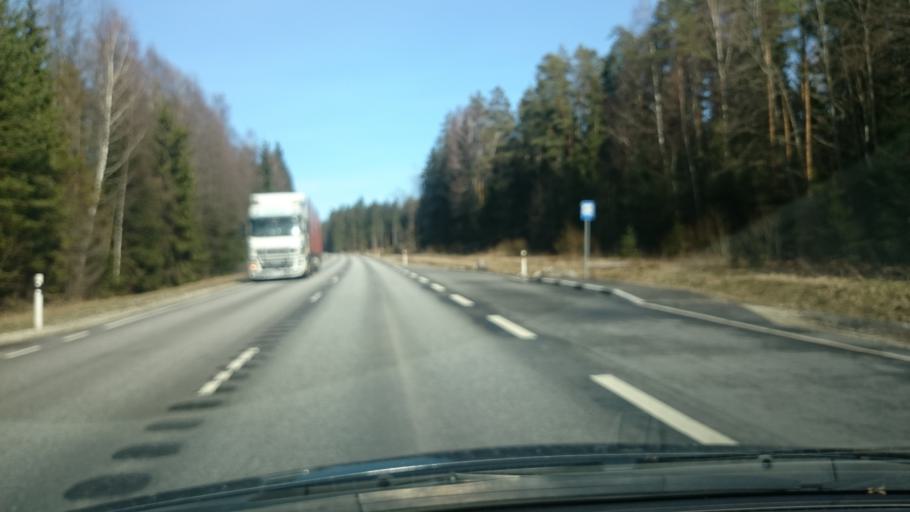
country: EE
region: Jaervamaa
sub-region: Tueri vald
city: Sarevere
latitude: 58.6991
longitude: 25.2586
